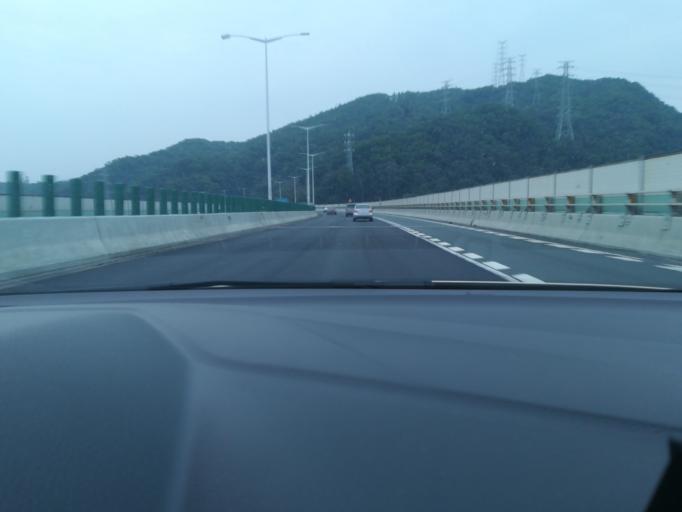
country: CN
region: Guangdong
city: Taihe
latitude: 23.2450
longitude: 113.3548
